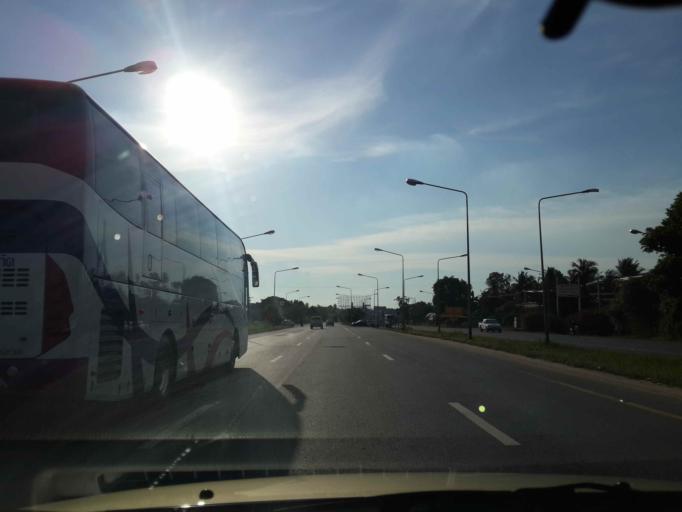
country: TH
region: Chon Buri
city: Bang Lamung
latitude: 12.9897
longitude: 100.9427
